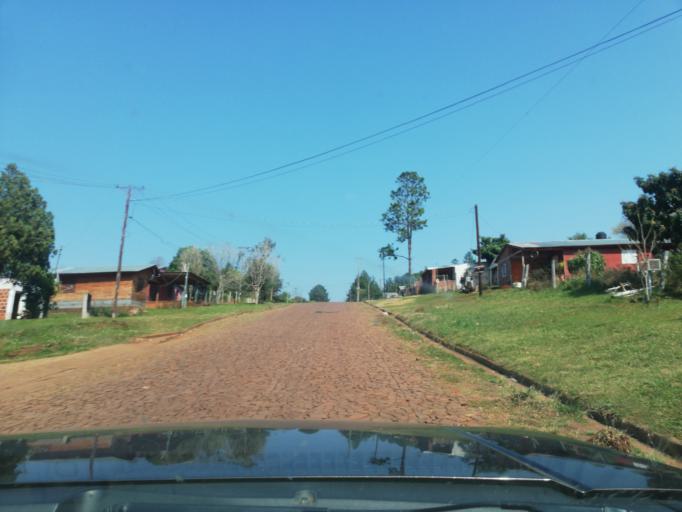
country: AR
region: Misiones
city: Bonpland
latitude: -27.4779
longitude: -55.4775
